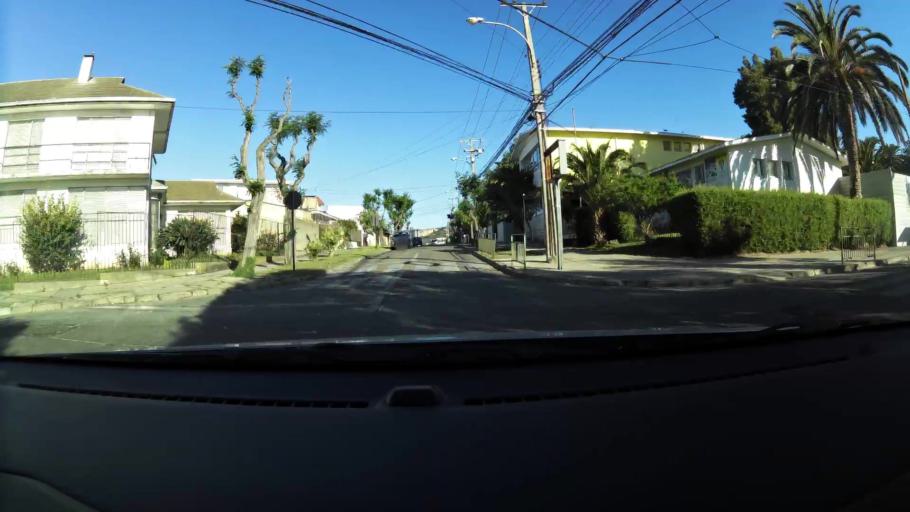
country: CL
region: Valparaiso
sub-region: Provincia de Valparaiso
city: Vina del Mar
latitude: -33.0302
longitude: -71.5811
